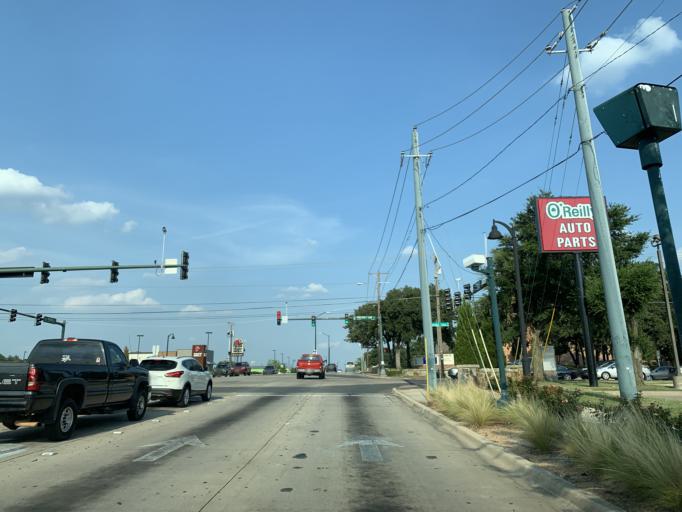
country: US
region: Texas
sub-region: Tarrant County
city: Hurst
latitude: 32.8236
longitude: -97.1869
